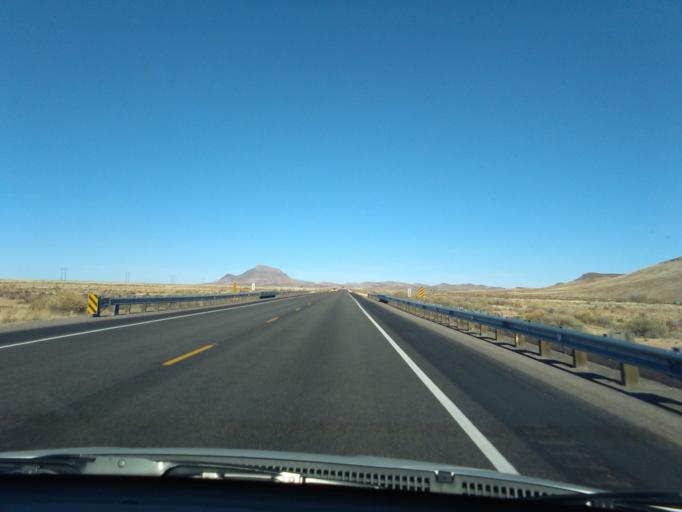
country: US
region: New Mexico
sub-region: Dona Ana County
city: Hatch
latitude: 32.5335
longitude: -107.4877
